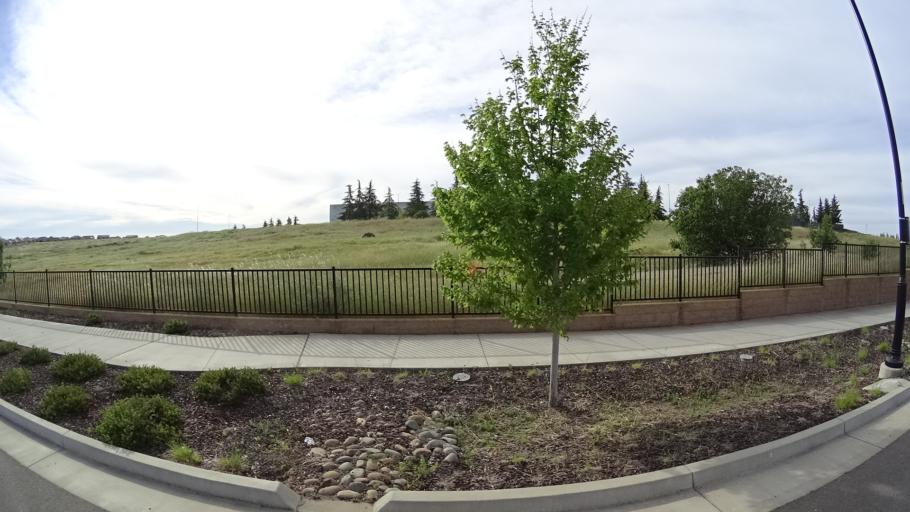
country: US
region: California
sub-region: Placer County
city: Rocklin
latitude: 38.8227
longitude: -121.2945
